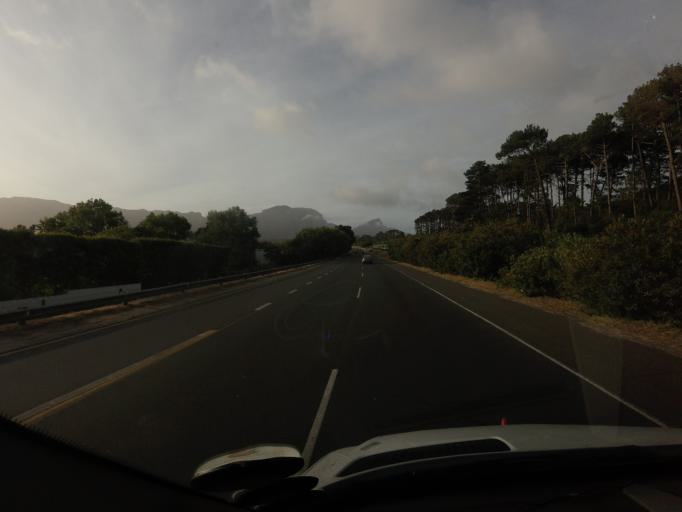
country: ZA
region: Western Cape
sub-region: City of Cape Town
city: Claremont
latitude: -34.0123
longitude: 18.4534
